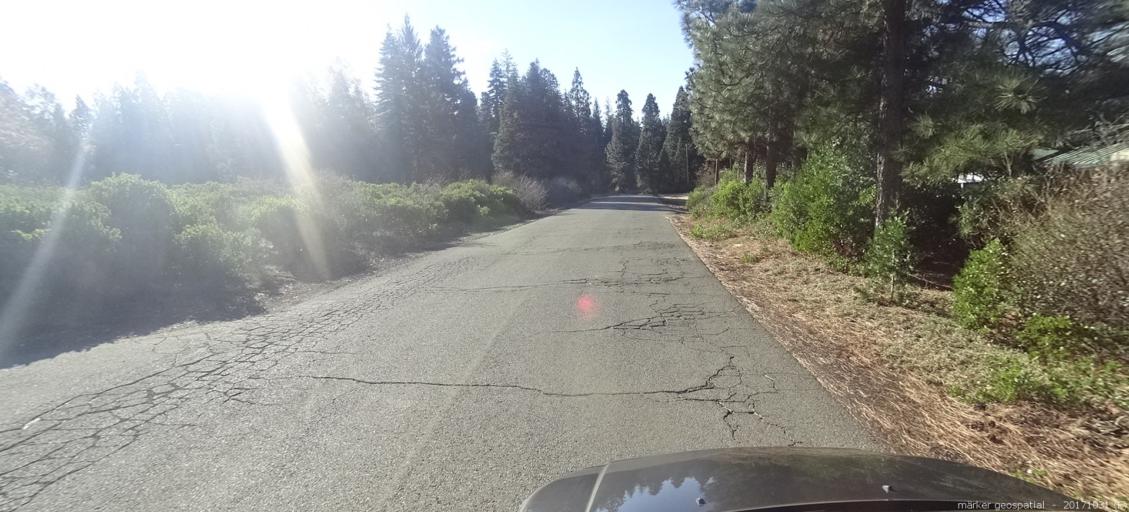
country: US
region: California
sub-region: Shasta County
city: Shingletown
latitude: 40.5152
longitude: -121.8129
